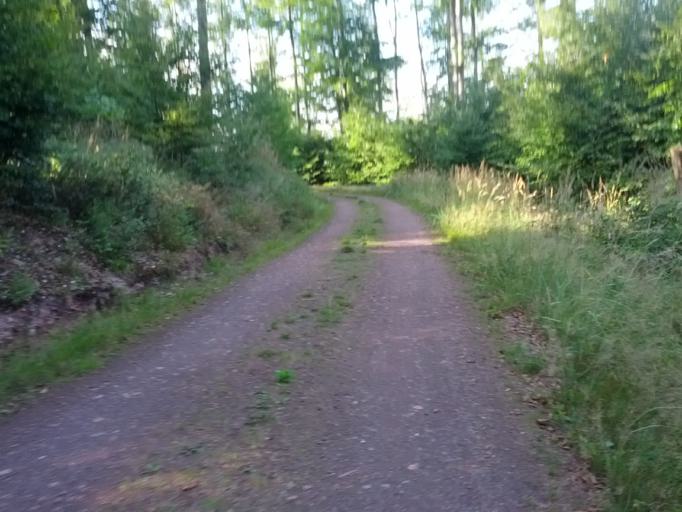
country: DE
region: Thuringia
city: Wolfsburg-Unkeroda
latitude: 50.9385
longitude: 10.3052
